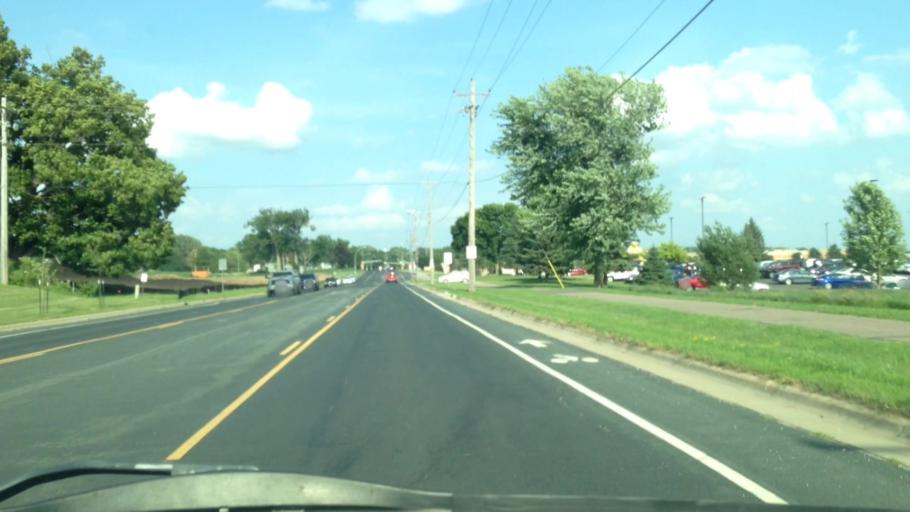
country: US
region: Minnesota
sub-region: Olmsted County
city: Rochester
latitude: 44.0435
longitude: -92.5098
